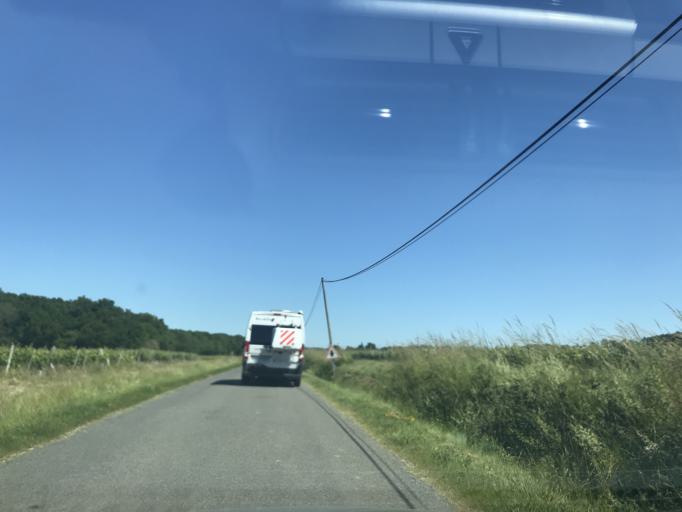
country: FR
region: Poitou-Charentes
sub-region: Departement de la Charente-Maritime
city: Mortagne-sur-Gironde
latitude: 45.4238
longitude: -0.7223
